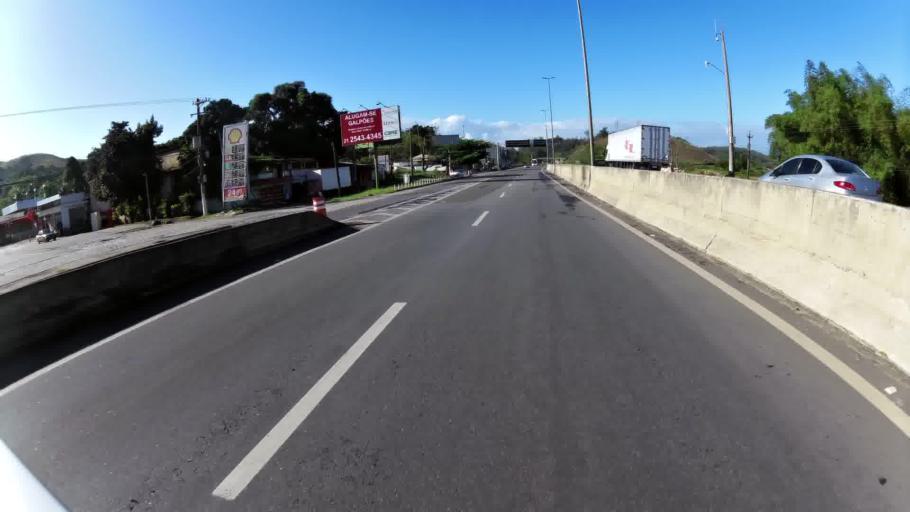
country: BR
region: Rio de Janeiro
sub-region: Petropolis
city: Petropolis
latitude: -22.6158
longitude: -43.2867
